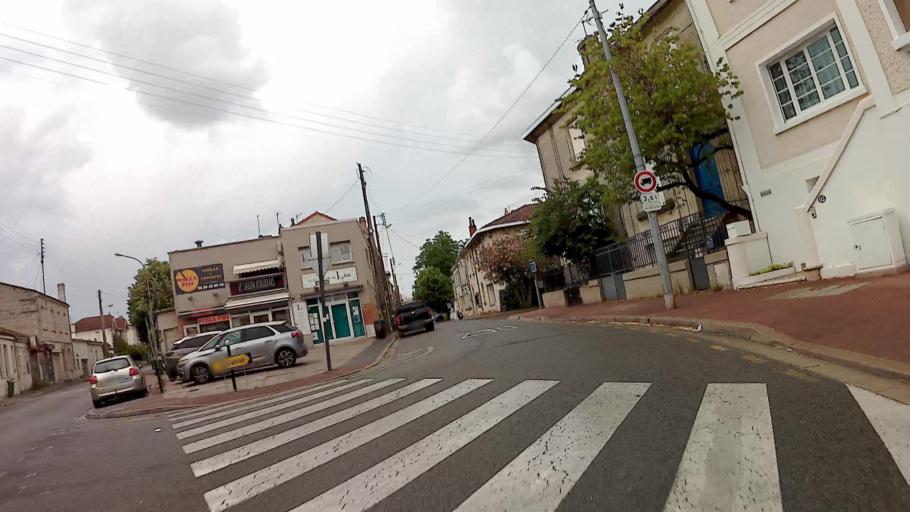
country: FR
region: Aquitaine
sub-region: Departement de la Gironde
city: Le Bouscat
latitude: 44.8565
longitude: -0.6023
